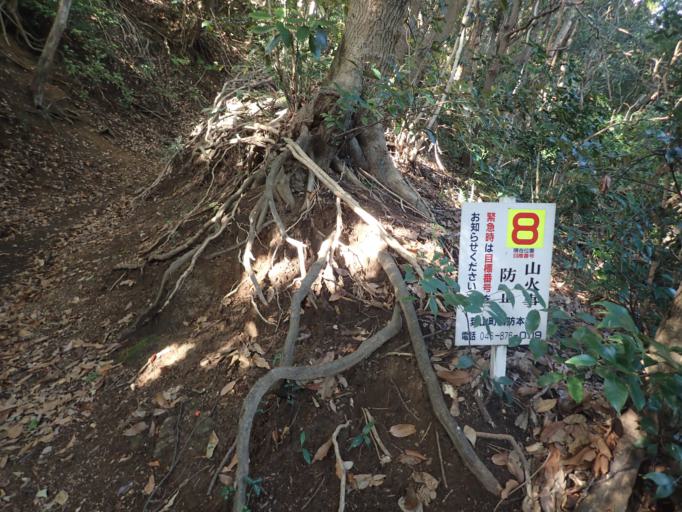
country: JP
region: Kanagawa
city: Hayama
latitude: 35.2712
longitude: 139.5893
